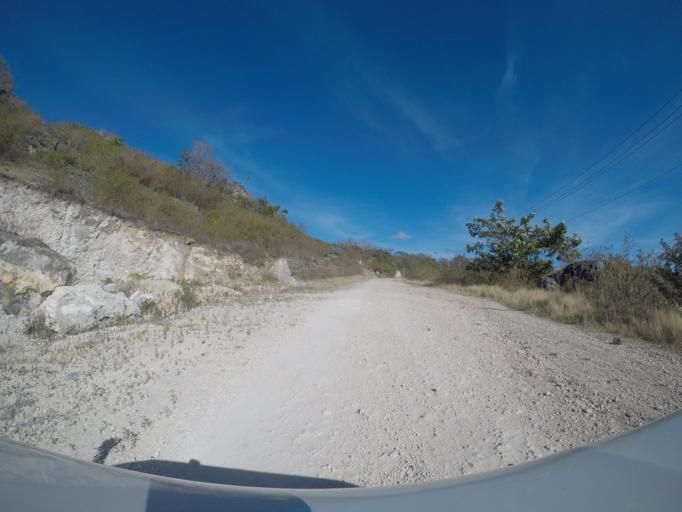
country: TL
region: Baucau
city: Baucau
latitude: -8.4502
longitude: 126.4289
